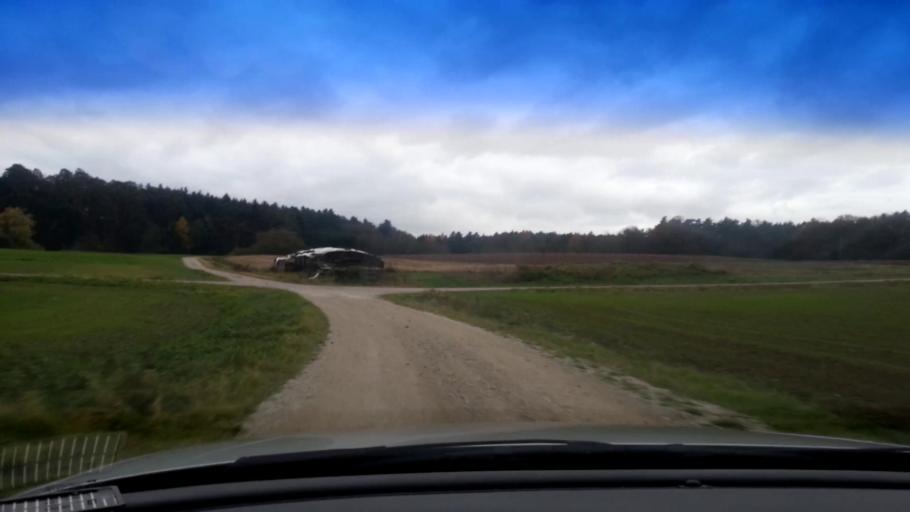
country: DE
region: Bavaria
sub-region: Upper Franconia
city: Walsdorf
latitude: 49.8577
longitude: 10.7960
